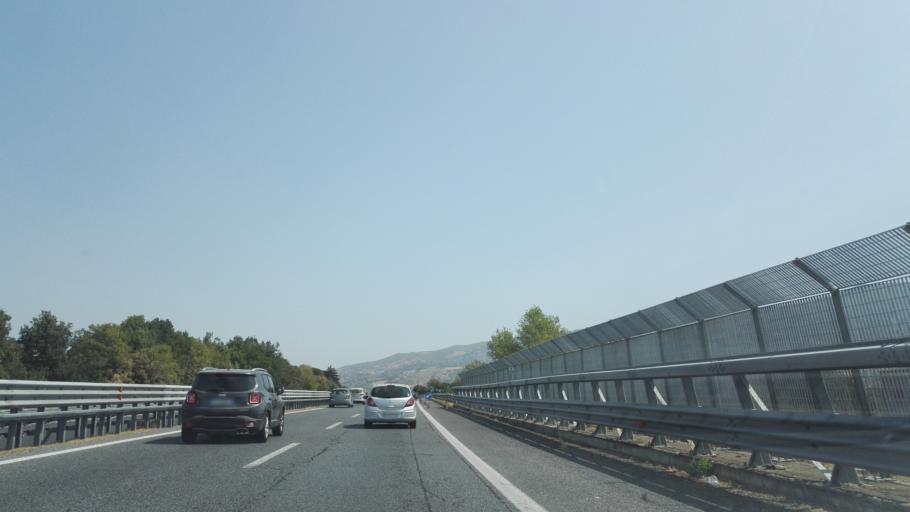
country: IT
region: Calabria
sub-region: Provincia di Cosenza
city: Settimo
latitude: 39.3874
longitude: 16.2387
